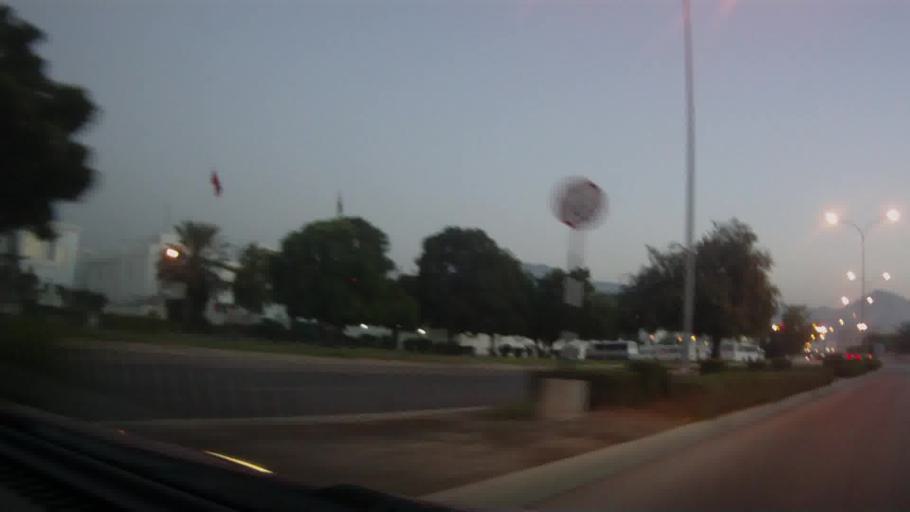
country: OM
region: Muhafazat Masqat
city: Bawshar
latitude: 23.6042
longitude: 58.4421
